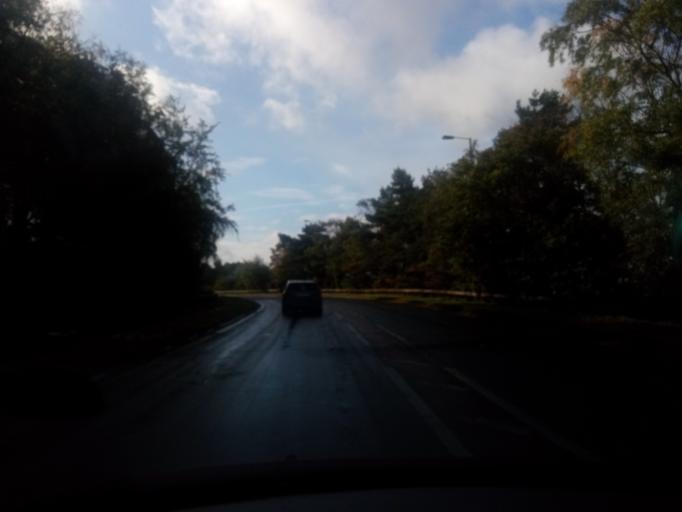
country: GB
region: England
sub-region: Cumbria
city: Carlisle
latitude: 54.9327
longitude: -2.9461
